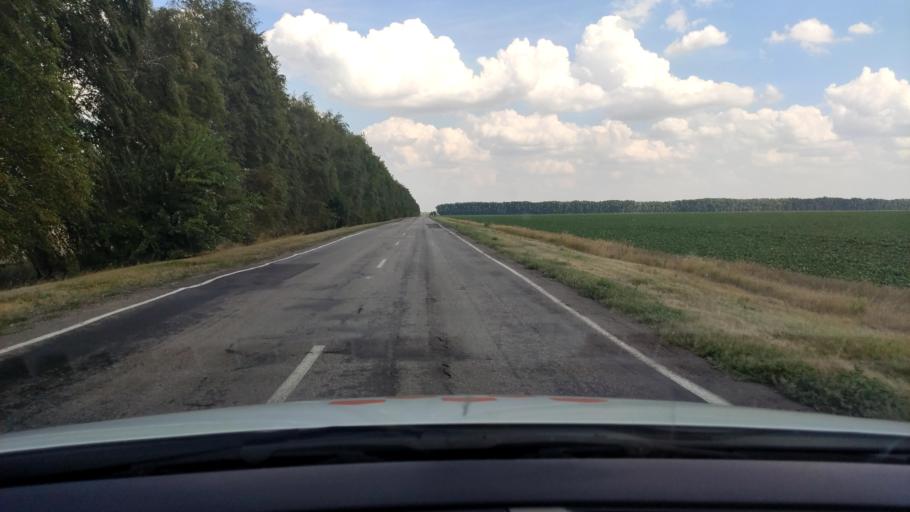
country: RU
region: Voronezj
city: Ertil'
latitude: 51.7882
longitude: 40.6087
